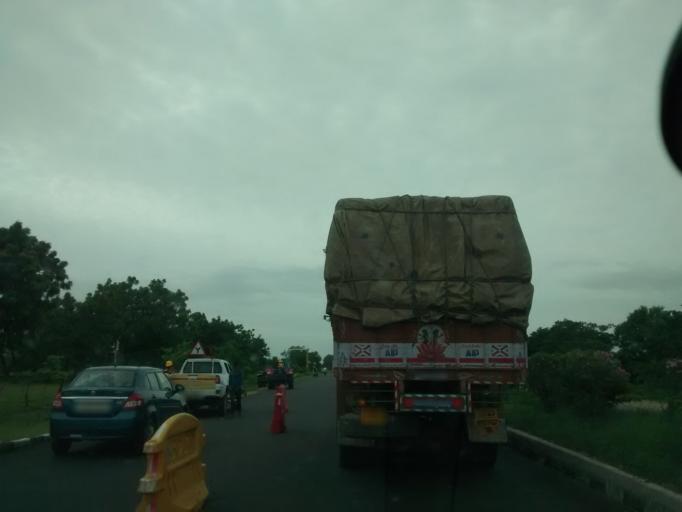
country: IN
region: Telangana
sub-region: Mahbubnagar
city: Wanparti
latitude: 16.3542
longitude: 77.9464
